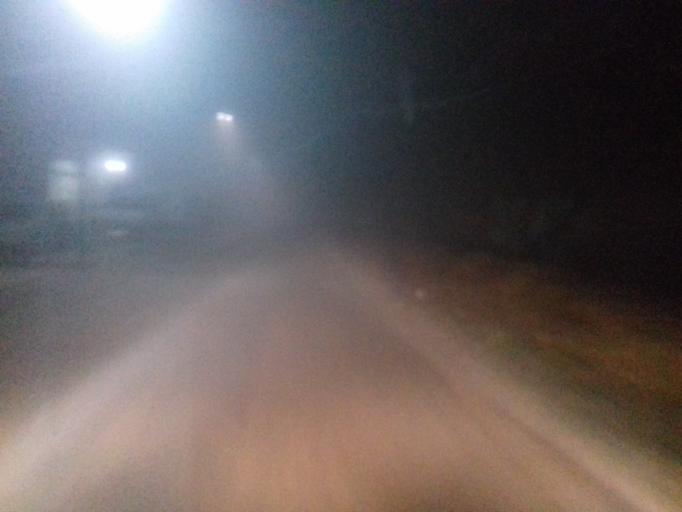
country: BA
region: Federation of Bosnia and Herzegovina
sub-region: Kanton Sarajevo
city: Sarajevo
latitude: 43.8330
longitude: 18.3140
